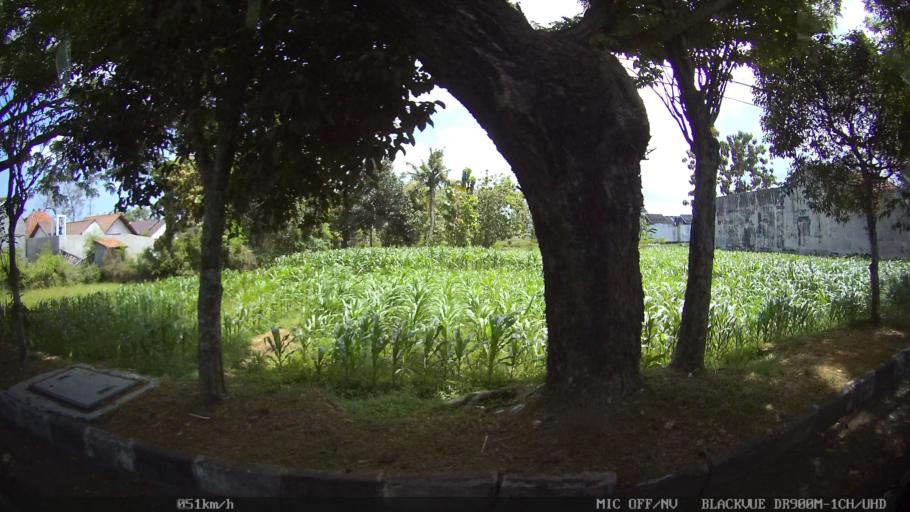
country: ID
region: Daerah Istimewa Yogyakarta
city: Bantul
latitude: -7.8820
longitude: 110.3359
